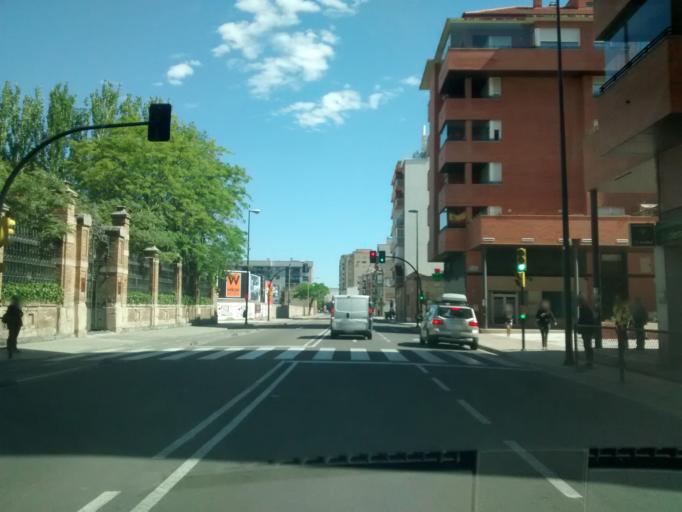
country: ES
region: Aragon
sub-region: Provincia de Zaragoza
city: Zaragoza
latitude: 41.6384
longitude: -0.8651
